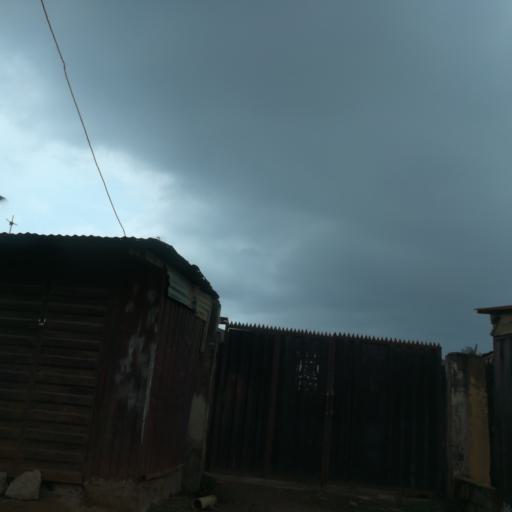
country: NG
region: Lagos
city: Agege
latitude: 6.5940
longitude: 3.2979
